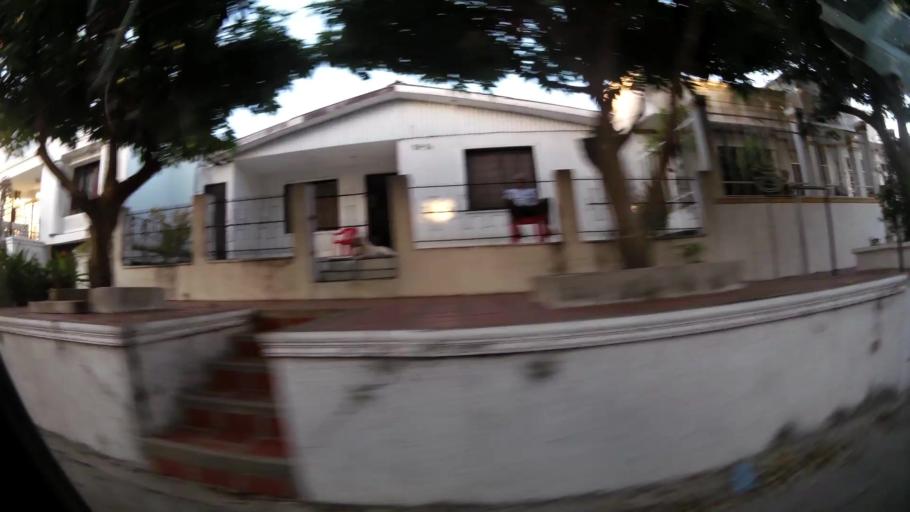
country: CO
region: Atlantico
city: Barranquilla
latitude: 10.9790
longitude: -74.8004
